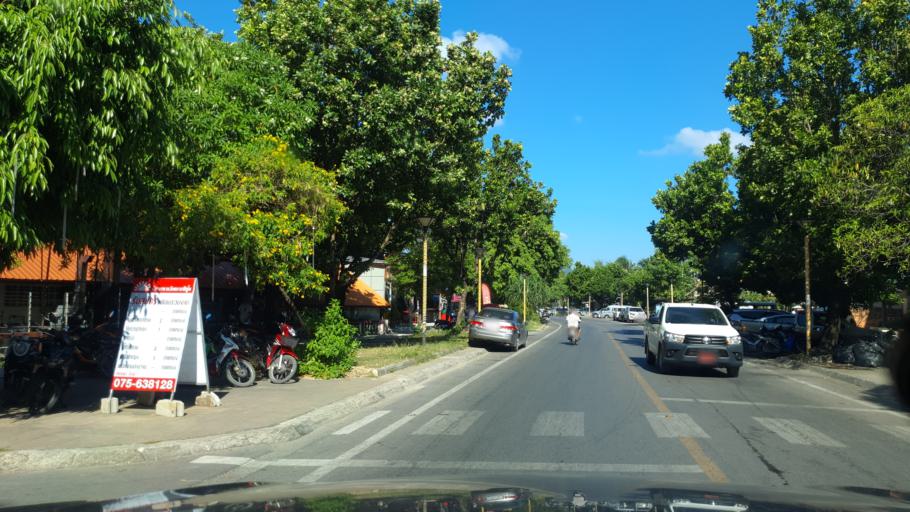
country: TH
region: Phangnga
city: Ban Ao Nang
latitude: 8.0385
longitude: 98.8162
